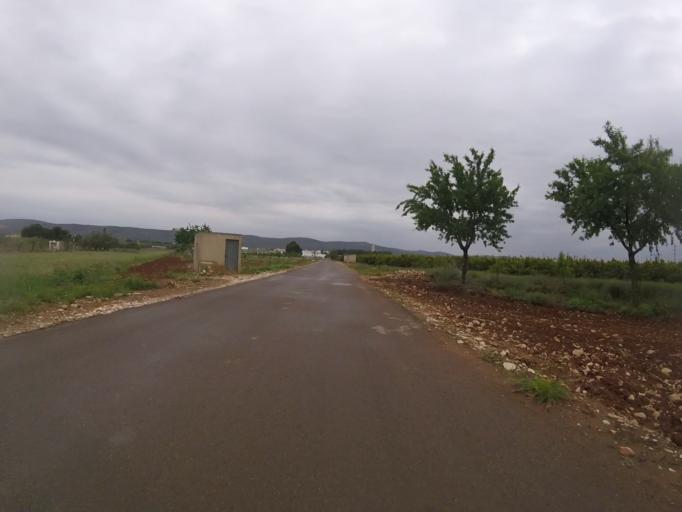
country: ES
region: Valencia
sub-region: Provincia de Castello
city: Alcala de Xivert
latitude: 40.2939
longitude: 0.2291
